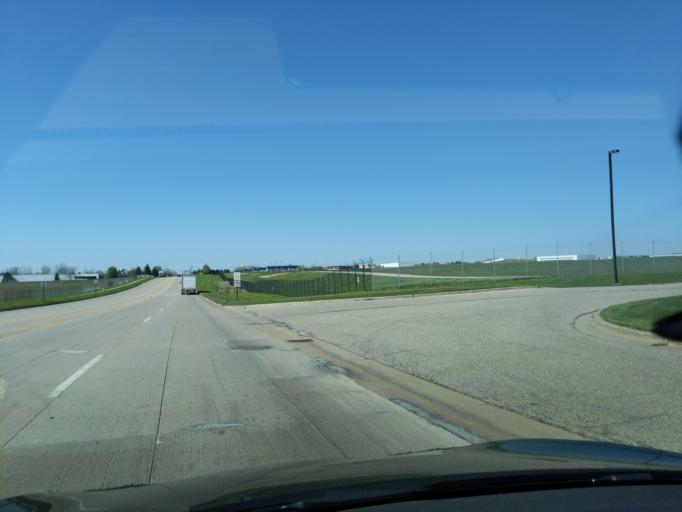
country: US
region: Michigan
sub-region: Kent County
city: Caledonia
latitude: 42.8741
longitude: -85.5466
